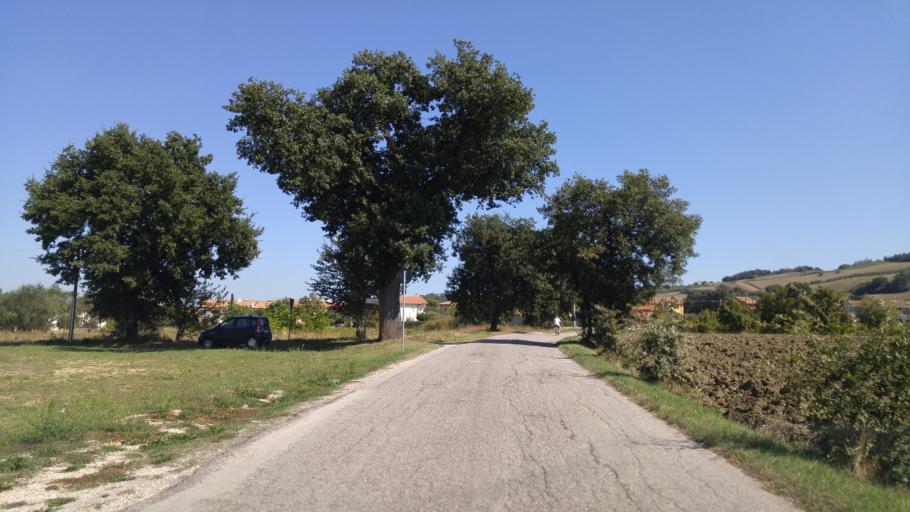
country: IT
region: The Marches
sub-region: Provincia di Pesaro e Urbino
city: Montemaggiore al Metauro
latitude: 43.7479
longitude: 12.9463
